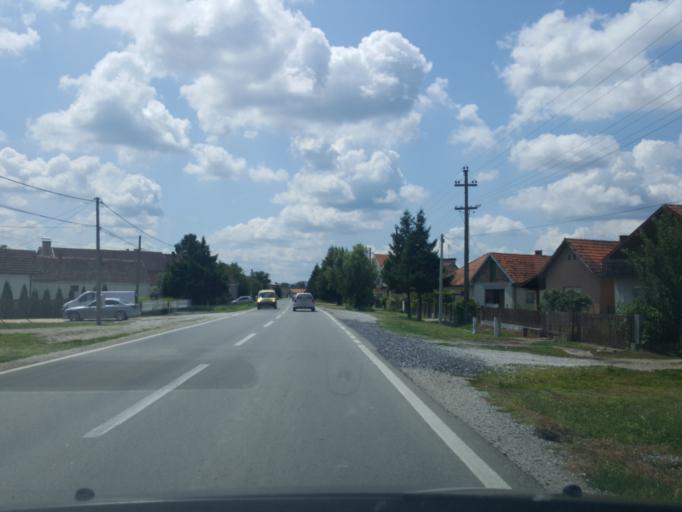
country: RS
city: Ribari
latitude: 44.7165
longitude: 19.4405
